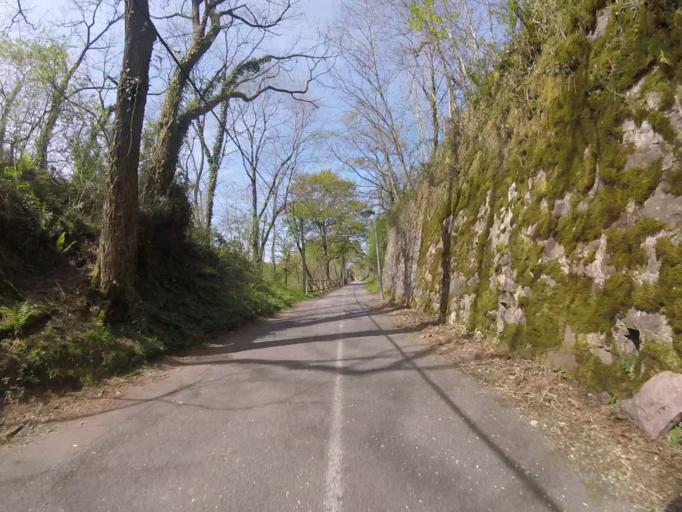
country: ES
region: Basque Country
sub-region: Provincia de Guipuzcoa
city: Irun
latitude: 43.2864
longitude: -1.8285
